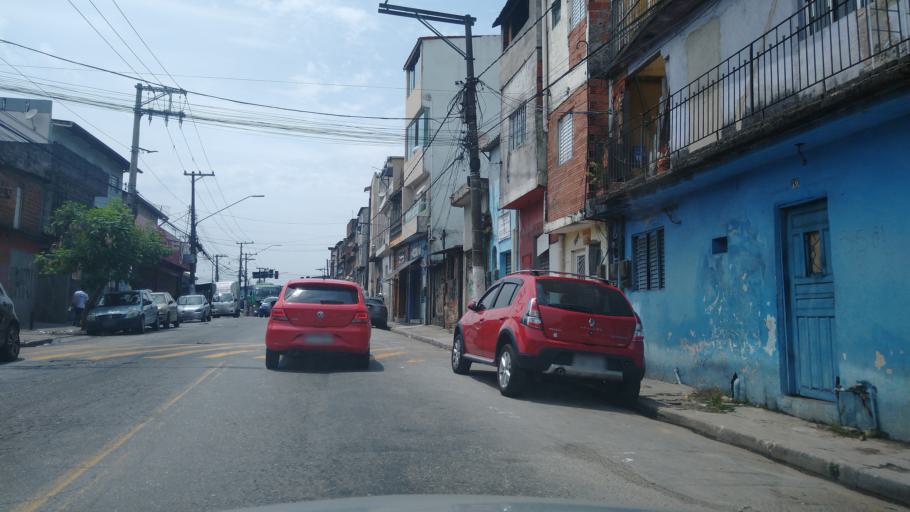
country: BR
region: Sao Paulo
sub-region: Caieiras
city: Caieiras
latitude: -23.4552
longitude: -46.6951
